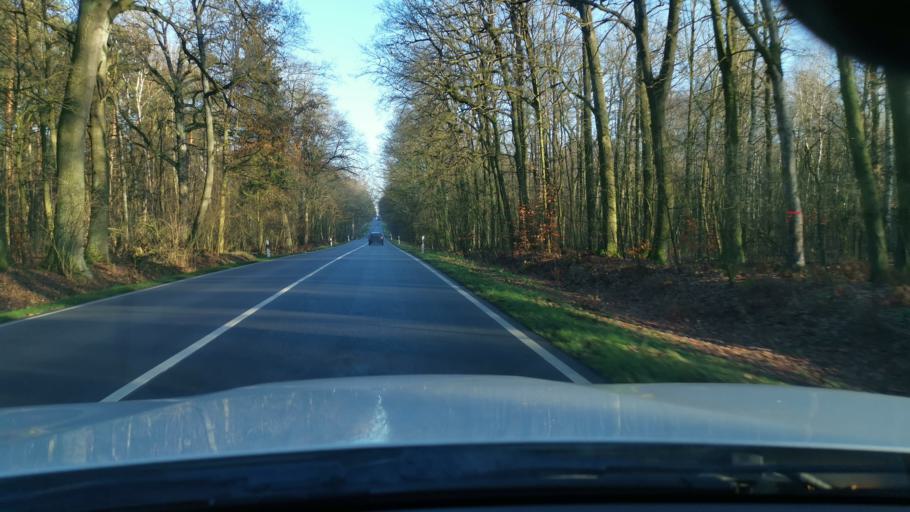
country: DE
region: Saxony-Anhalt
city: Kropstadt
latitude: 51.9454
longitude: 12.7254
